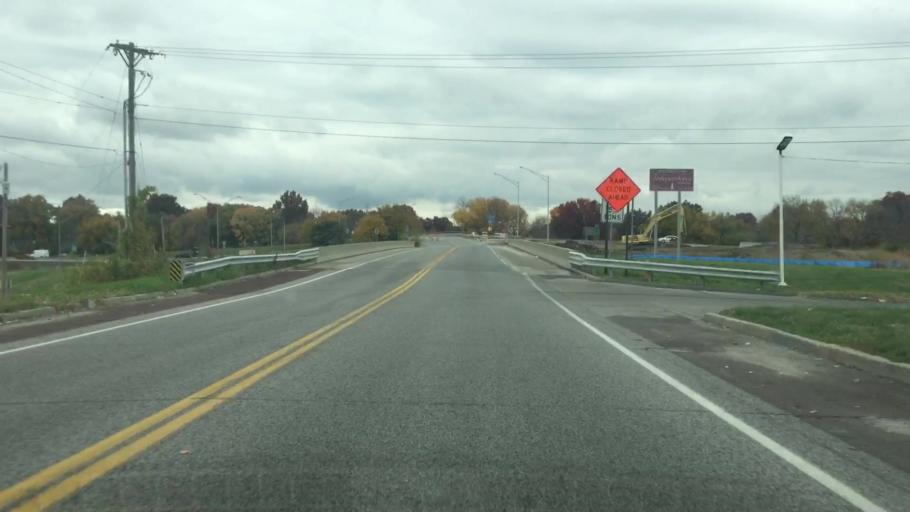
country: US
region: Missouri
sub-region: Jackson County
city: Raytown
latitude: 39.0450
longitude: -94.4389
